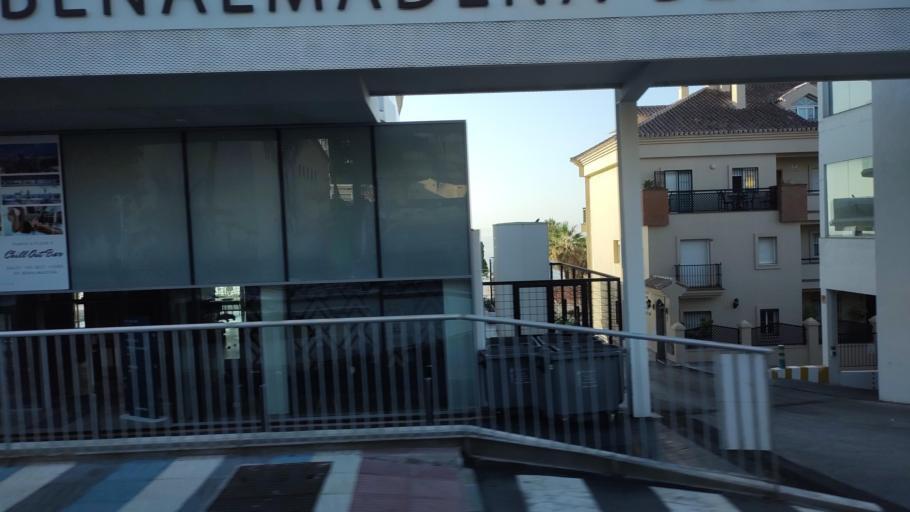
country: ES
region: Andalusia
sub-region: Provincia de Malaga
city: Torremolinos
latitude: 36.5943
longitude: -4.5216
